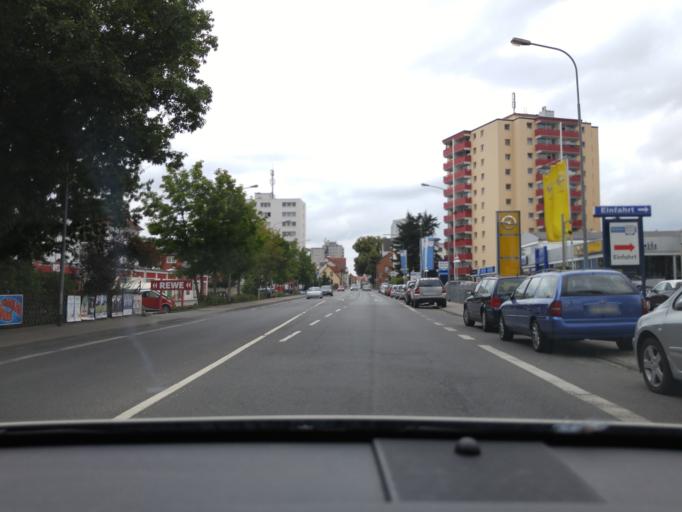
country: DE
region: Hesse
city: Langen
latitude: 49.9815
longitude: 8.6780
